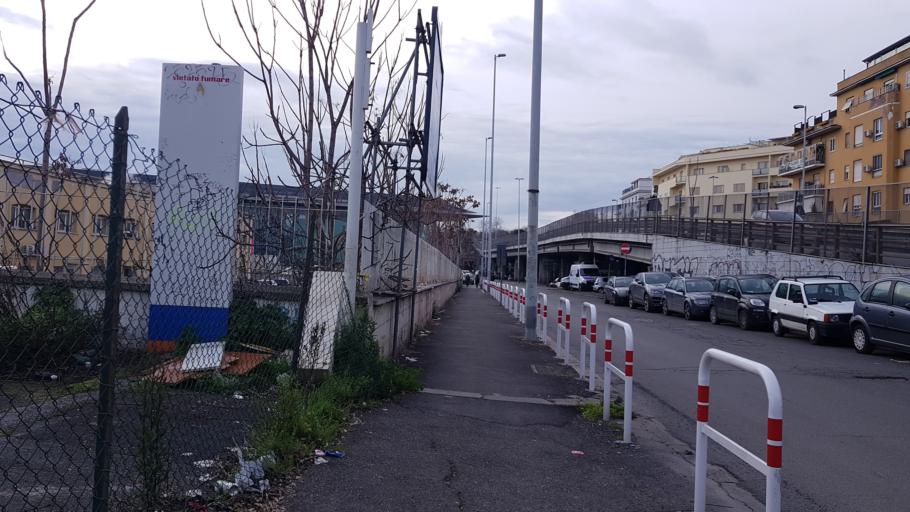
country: IT
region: Latium
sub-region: Citta metropolitana di Roma Capitale
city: Rome
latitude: 41.9120
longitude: 12.5285
